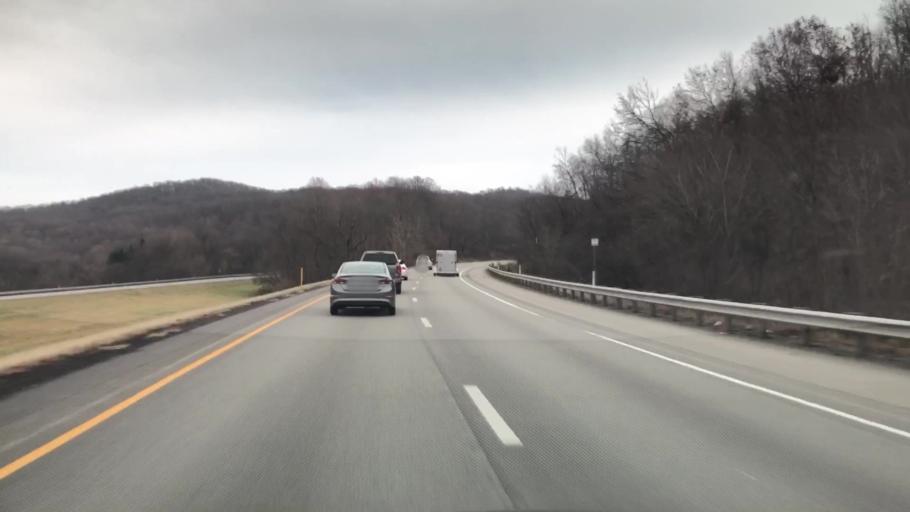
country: US
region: Pennsylvania
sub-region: Butler County
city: Zelienople
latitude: 40.7539
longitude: -80.1104
